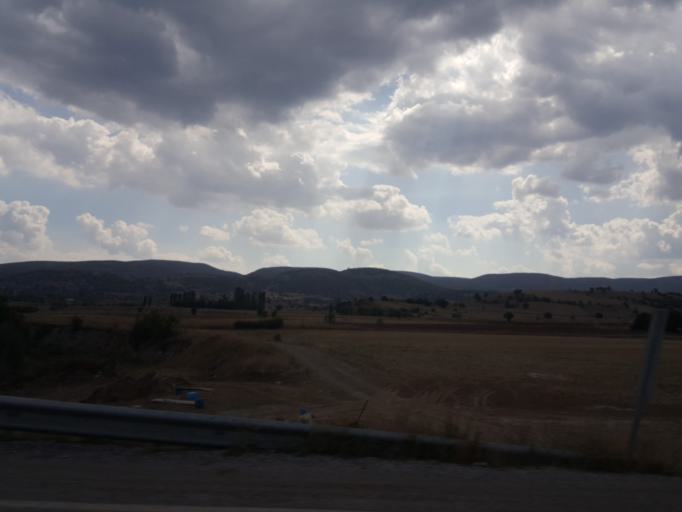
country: TR
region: Yozgat
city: Aydincik
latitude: 40.1761
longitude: 35.3776
